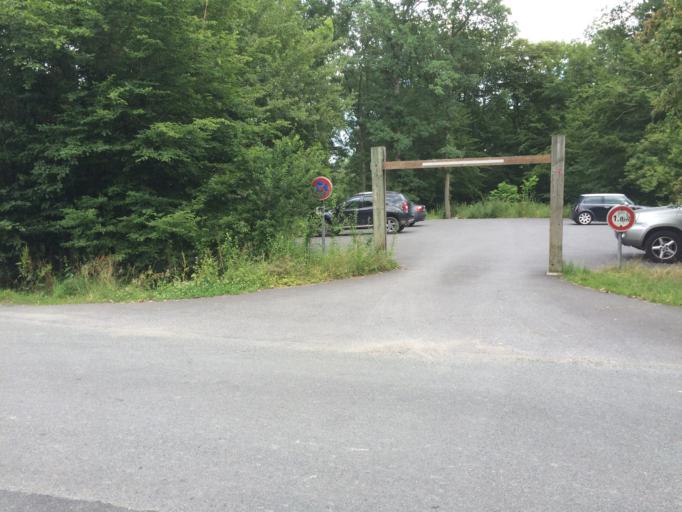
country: FR
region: Ile-de-France
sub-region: Departement de l'Essonne
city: Brunoy
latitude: 48.6827
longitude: 2.4892
